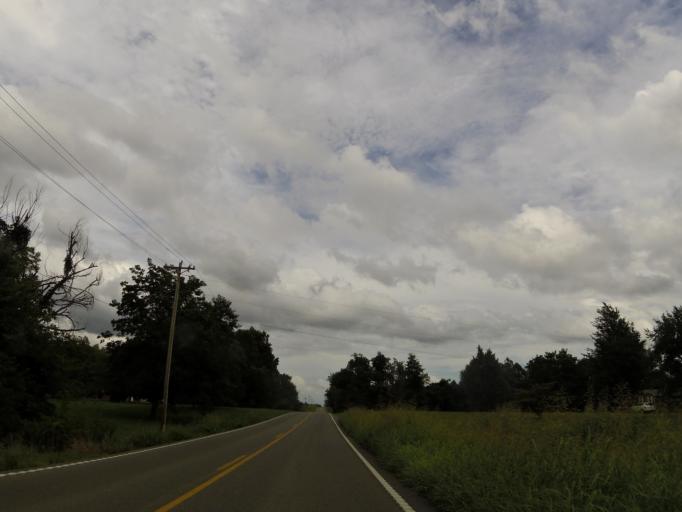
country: US
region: Kentucky
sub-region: Ballard County
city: La Center
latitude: 36.9908
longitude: -88.9191
